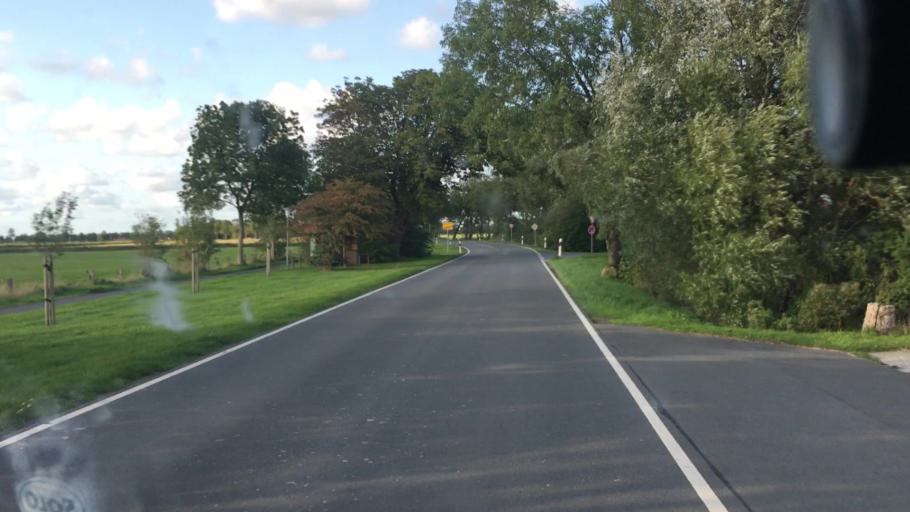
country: DE
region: Lower Saxony
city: Jever
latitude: 53.5991
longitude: 7.8693
